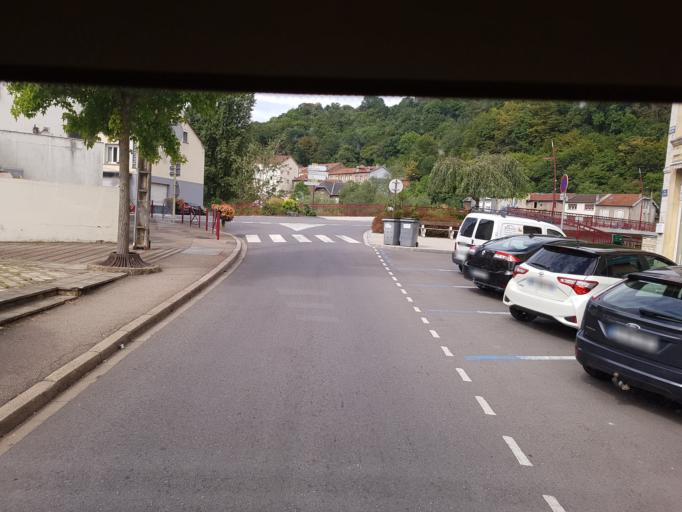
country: FR
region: Lorraine
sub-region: Departement de Meurthe-et-Moselle
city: Homecourt
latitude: 49.2276
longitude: 5.9929
